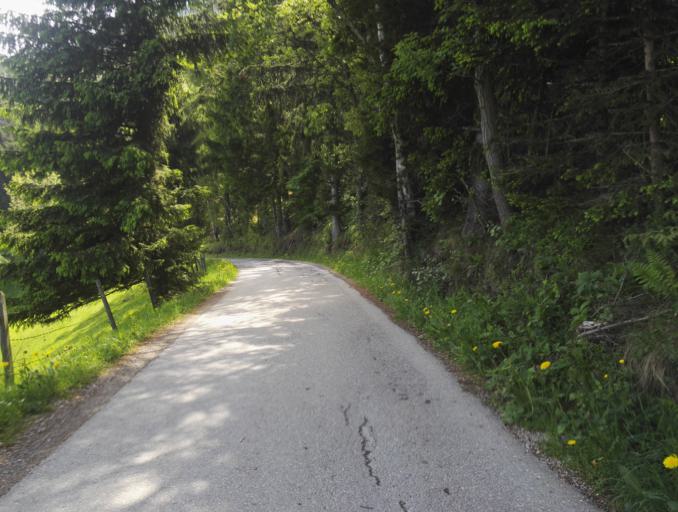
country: AT
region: Styria
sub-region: Politischer Bezirk Graz-Umgebung
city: Semriach
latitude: 47.1937
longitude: 15.4295
